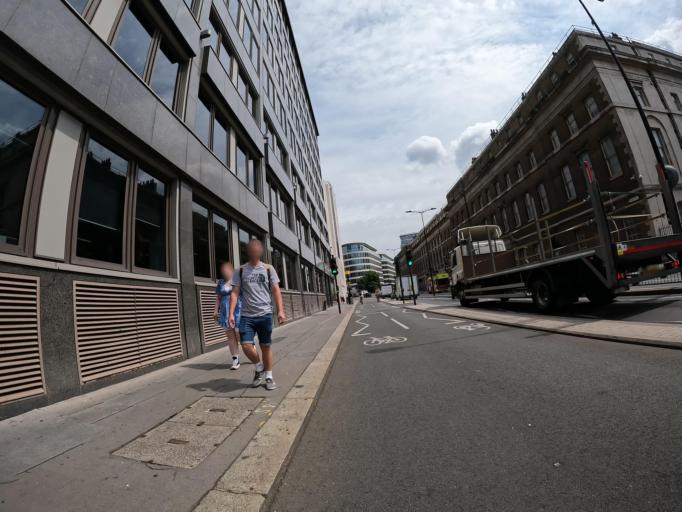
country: GB
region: England
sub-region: Greater London
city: Hendon
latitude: 51.6127
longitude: -0.1803
